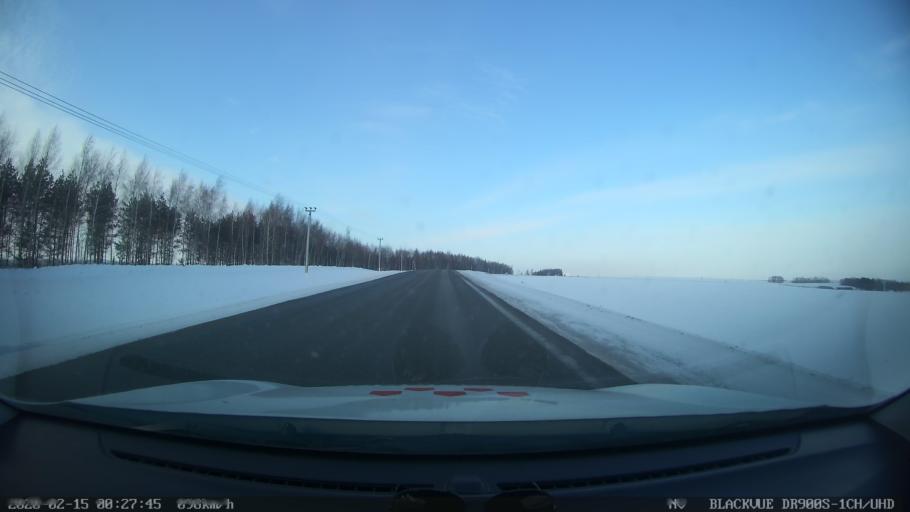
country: RU
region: Tatarstan
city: Verkhniy Uslon
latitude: 55.6327
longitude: 48.8726
